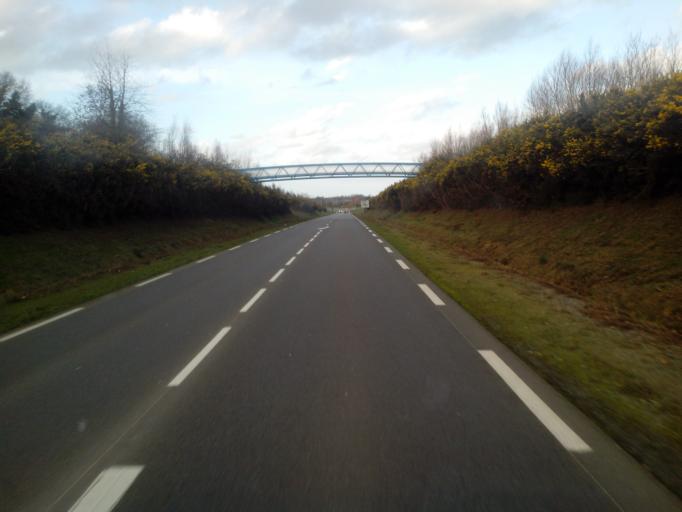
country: FR
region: Brittany
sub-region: Departement d'Ille-et-Vilaine
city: Pleurtuit
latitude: 48.5890
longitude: -2.0690
